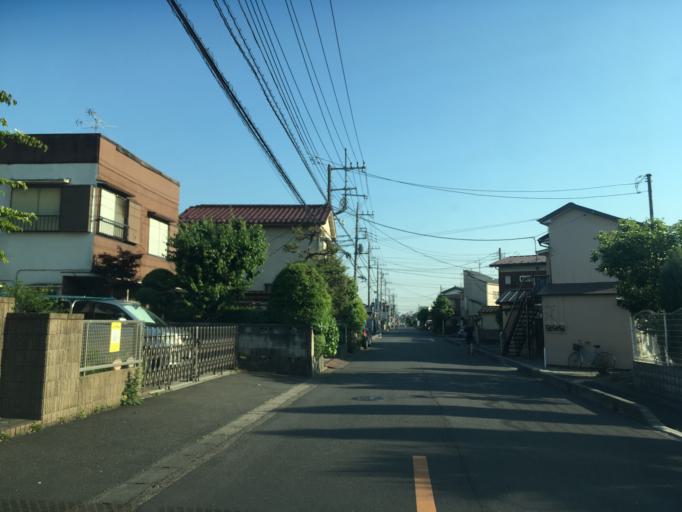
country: JP
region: Saitama
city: Koshigaya
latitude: 35.8649
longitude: 139.8030
